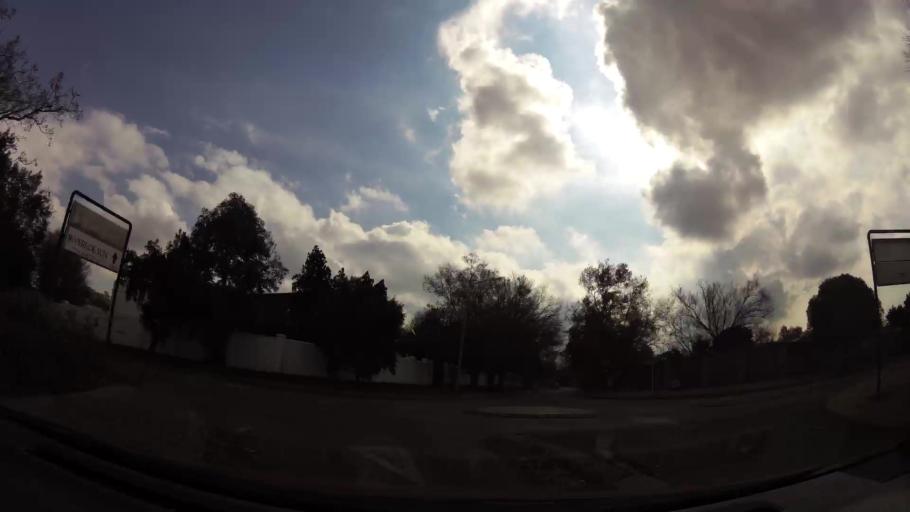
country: ZA
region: Gauteng
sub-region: Sedibeng District Municipality
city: Vanderbijlpark
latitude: -26.7395
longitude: 27.8267
